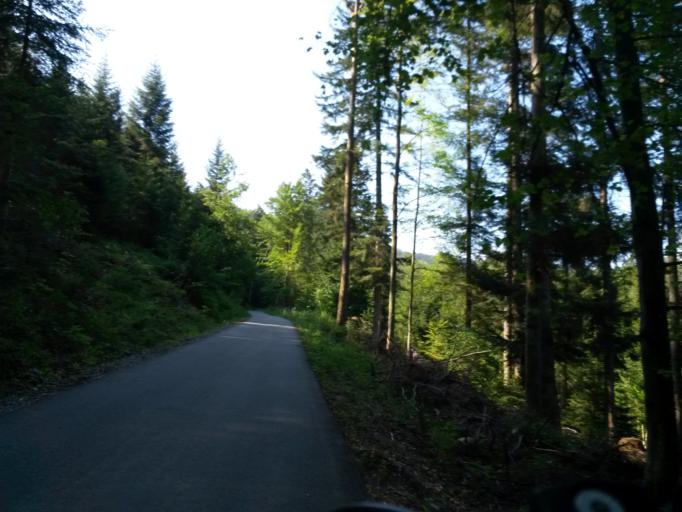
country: DE
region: Baden-Wuerttemberg
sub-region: Karlsruhe Region
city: Bad Wildbad
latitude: 48.7122
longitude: 8.5443
